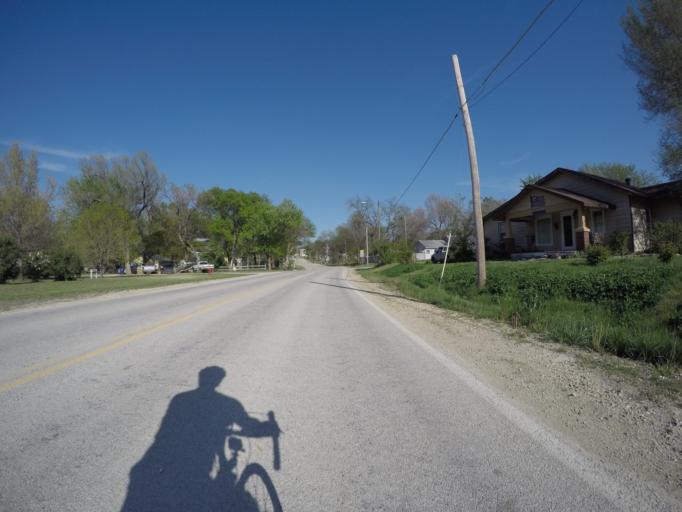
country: US
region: Kansas
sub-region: Riley County
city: Fort Riley North
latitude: 39.2990
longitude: -96.8303
